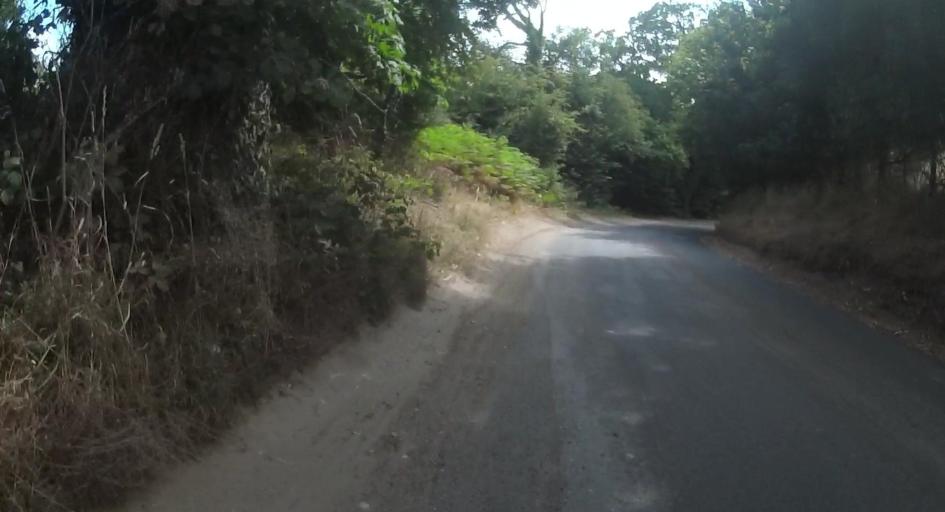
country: GB
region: England
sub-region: Dorset
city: Bovington Camp
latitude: 50.6942
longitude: -2.2707
